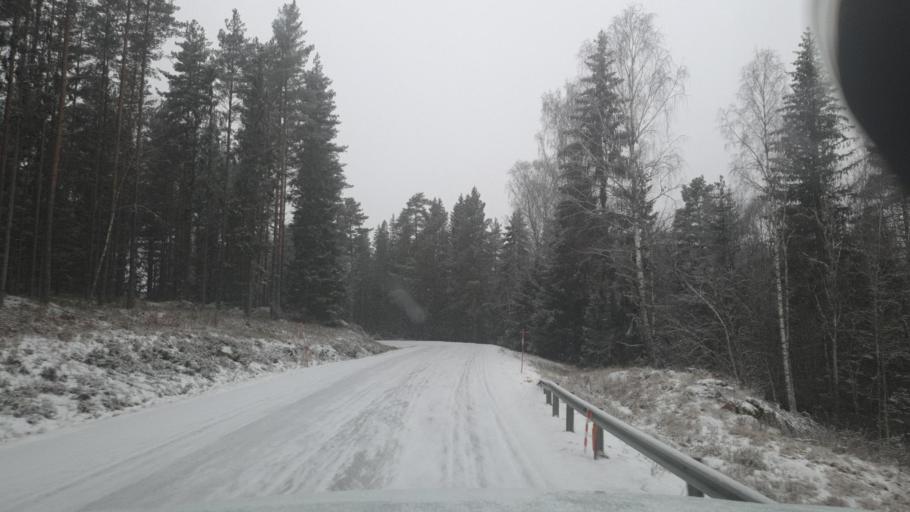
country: SE
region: Vaermland
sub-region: Grums Kommun
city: Grums
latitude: 59.5134
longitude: 12.8596
